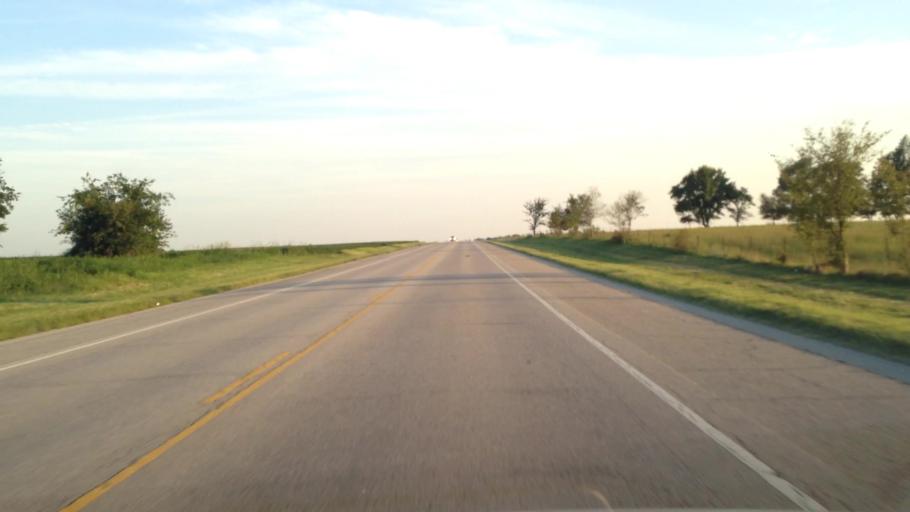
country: US
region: Oklahoma
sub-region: Ottawa County
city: Afton
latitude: 36.6489
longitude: -94.9814
